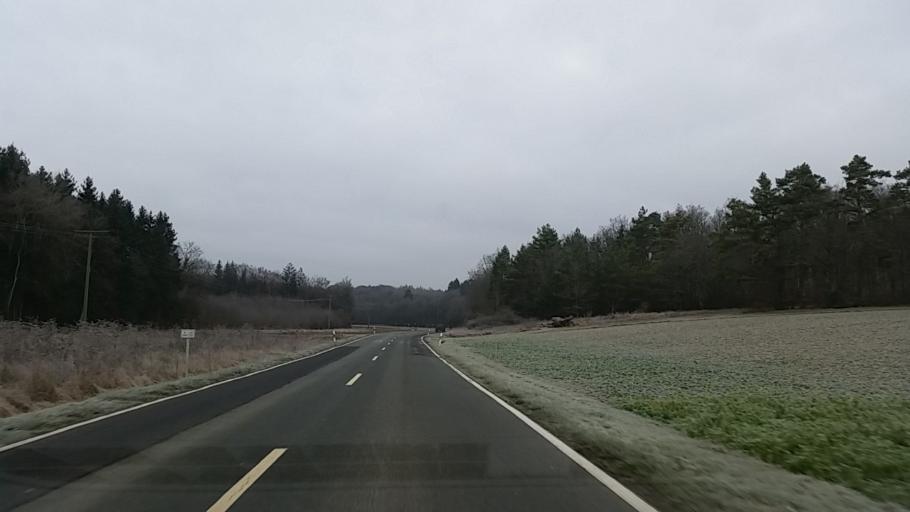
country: DE
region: Bavaria
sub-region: Regierungsbezirk Unterfranken
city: Fuchsstadt
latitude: 50.0751
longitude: 9.9167
